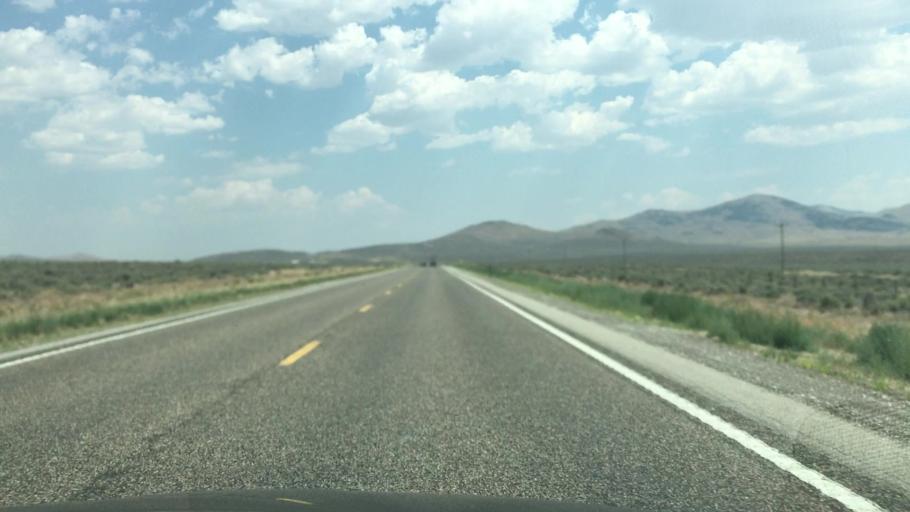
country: US
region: Nevada
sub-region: Elko County
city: Wells
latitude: 41.1596
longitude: -114.8941
